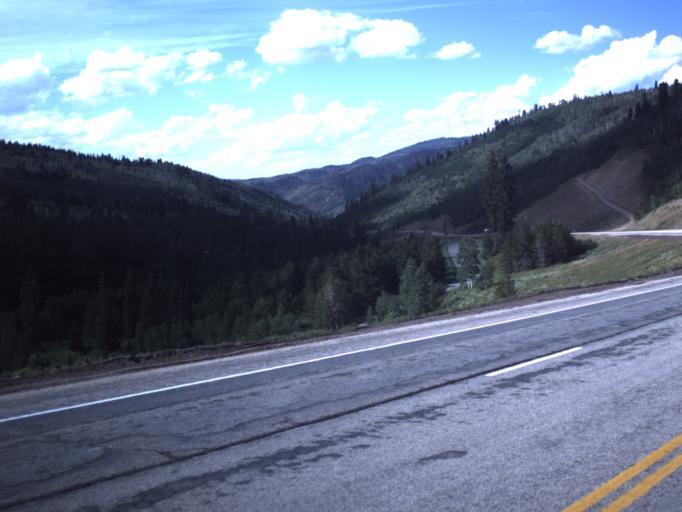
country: US
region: Utah
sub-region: Wasatch County
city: Heber
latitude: 40.3102
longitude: -111.2573
